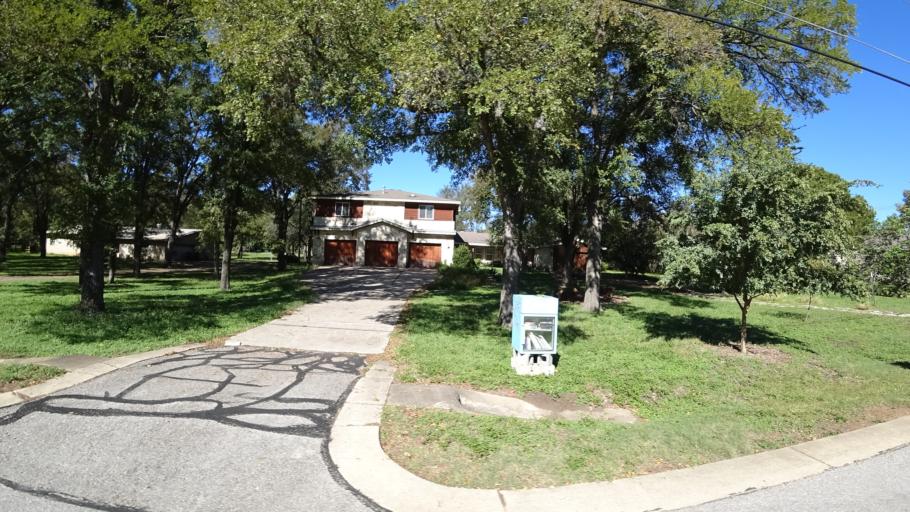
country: US
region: Texas
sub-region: Travis County
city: Rollingwood
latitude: 30.2269
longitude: -97.8083
